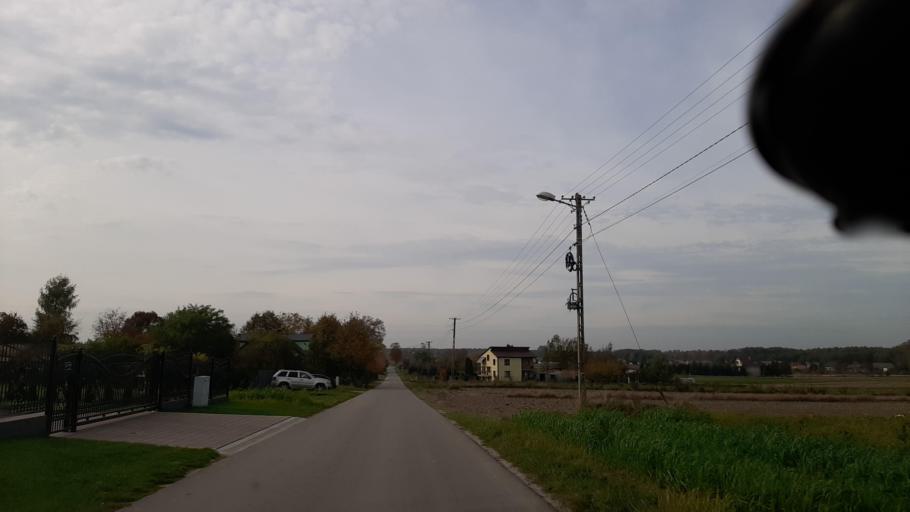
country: PL
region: Lublin Voivodeship
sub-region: Powiat lubelski
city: Garbow
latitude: 51.3918
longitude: 22.3208
